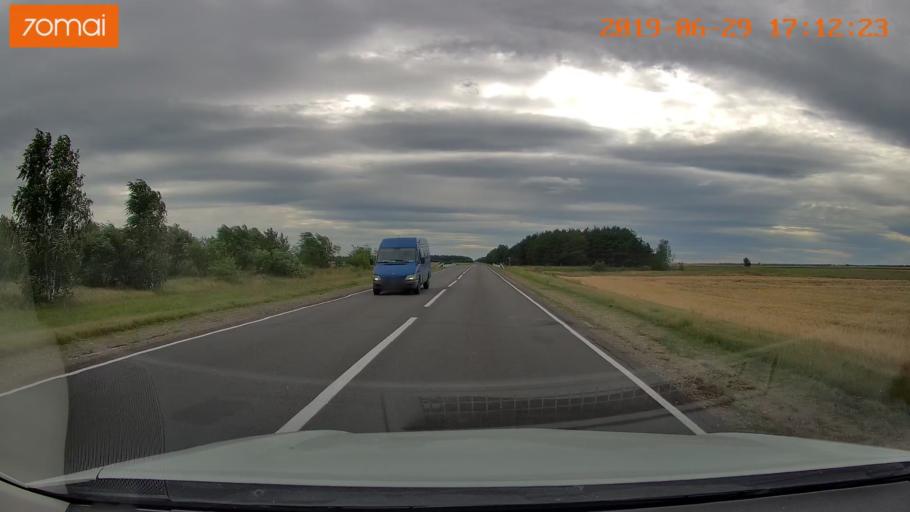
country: BY
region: Brest
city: Asnyezhytsy
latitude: 52.2692
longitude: 26.3580
